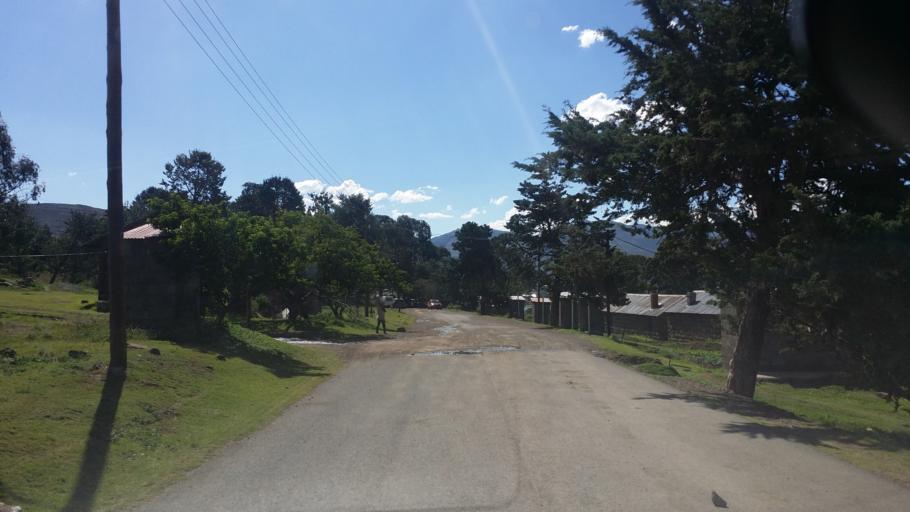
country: LS
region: Mokhotlong
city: Mokhotlong
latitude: -29.2903
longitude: 29.0679
